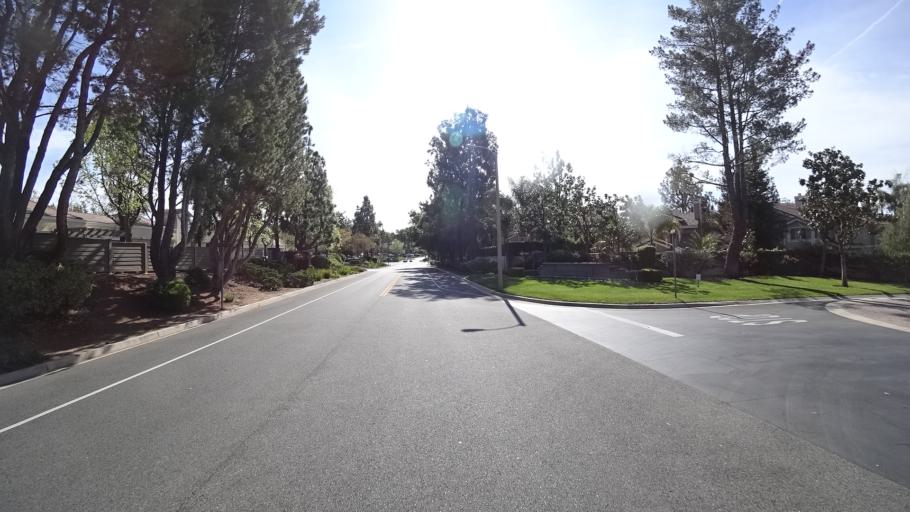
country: US
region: California
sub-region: Ventura County
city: Oak Park
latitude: 34.1833
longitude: -118.7880
